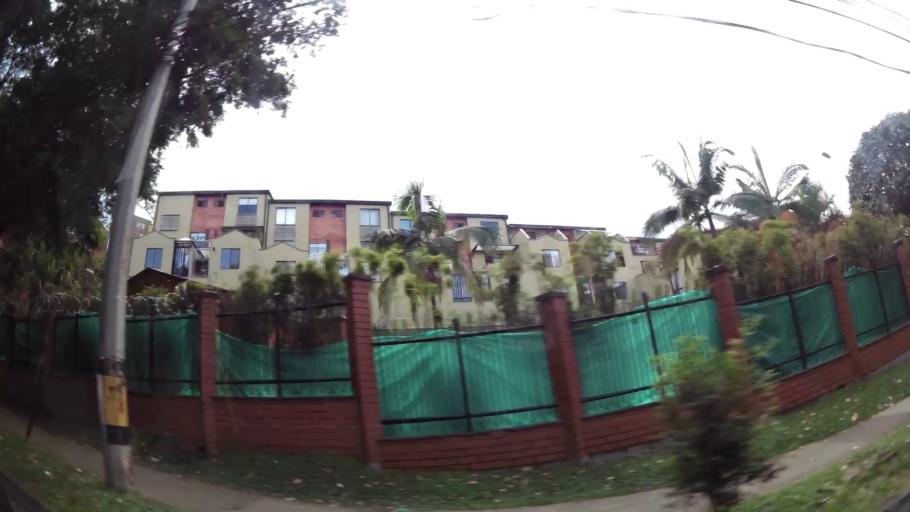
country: CO
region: Antioquia
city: Envigado
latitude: 6.1631
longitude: -75.5861
